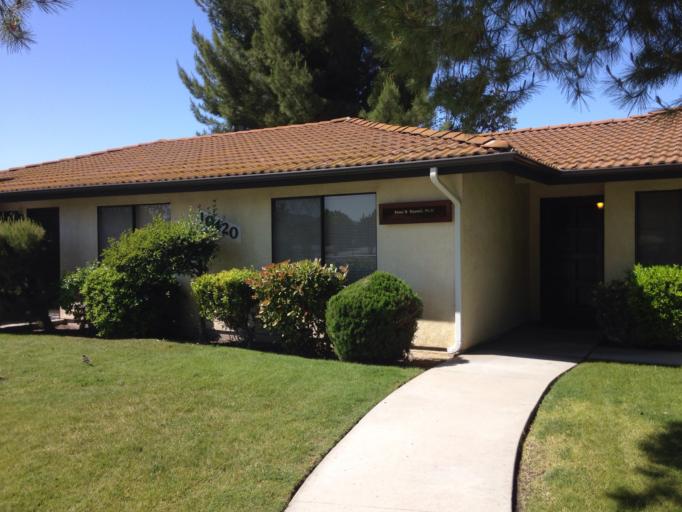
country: US
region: California
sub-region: San Luis Obispo County
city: Atascadero
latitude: 35.4605
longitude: -120.6442
